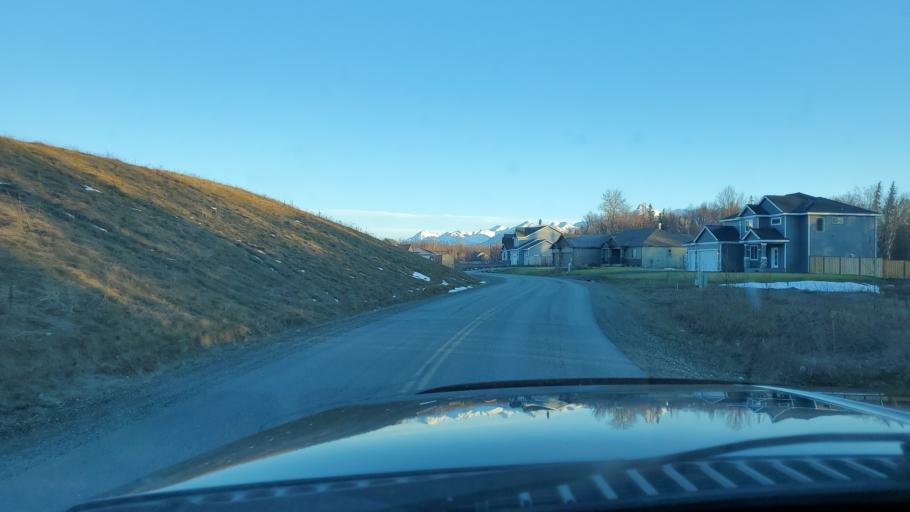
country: US
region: Alaska
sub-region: Matanuska-Susitna Borough
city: Gateway
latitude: 61.5862
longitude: -149.2618
